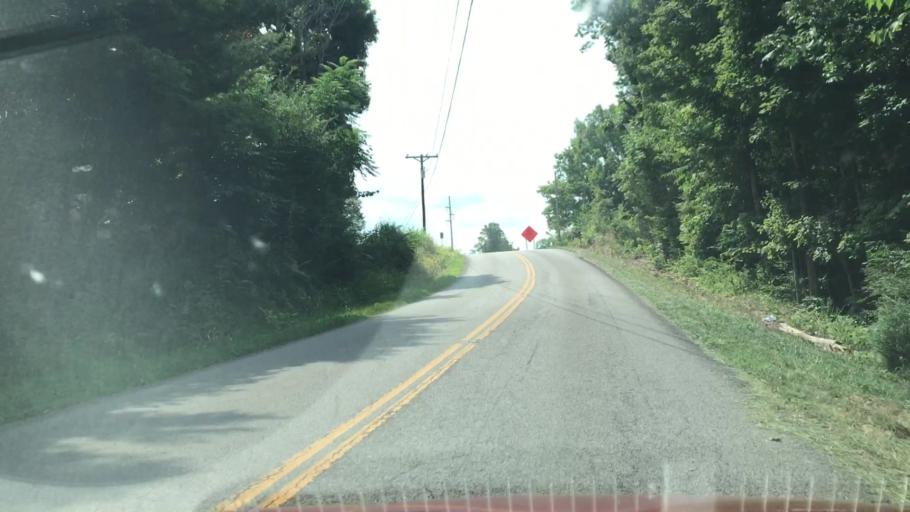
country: US
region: Kentucky
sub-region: Barren County
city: Glasgow
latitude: 36.8984
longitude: -85.8594
